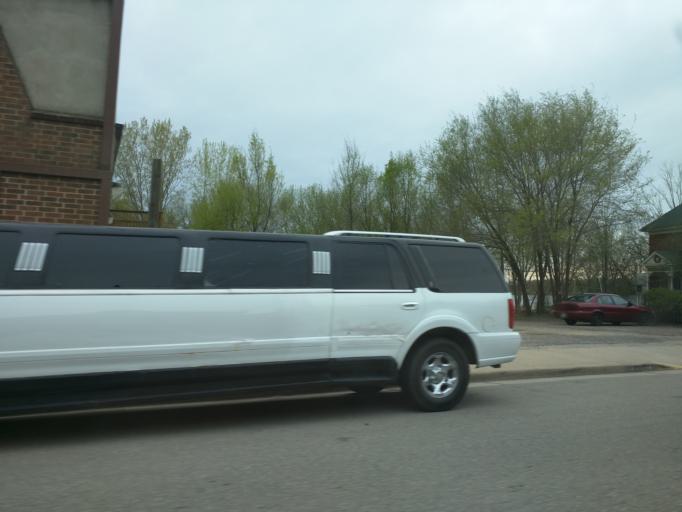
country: US
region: Minnesota
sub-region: Wabasha County
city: Lake City
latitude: 44.5608
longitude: -92.3100
